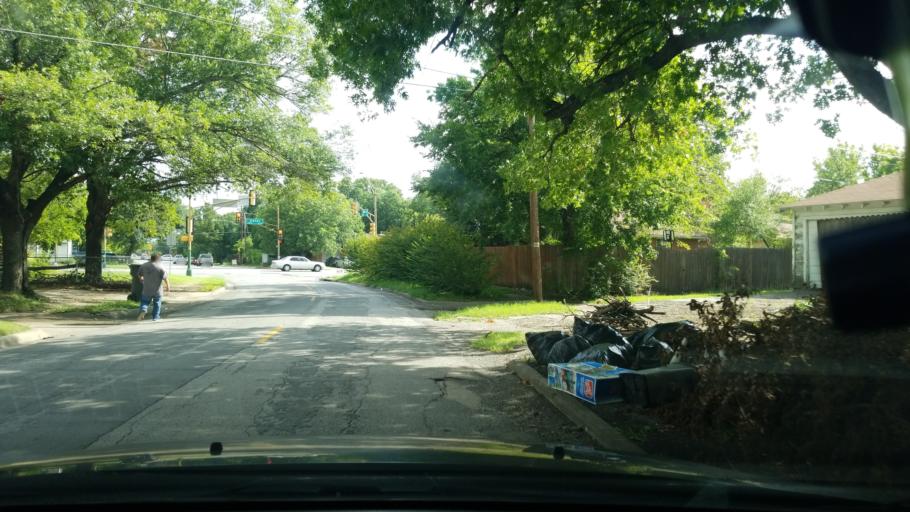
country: US
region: Texas
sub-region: Dallas County
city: Mesquite
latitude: 32.8208
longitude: -96.6682
